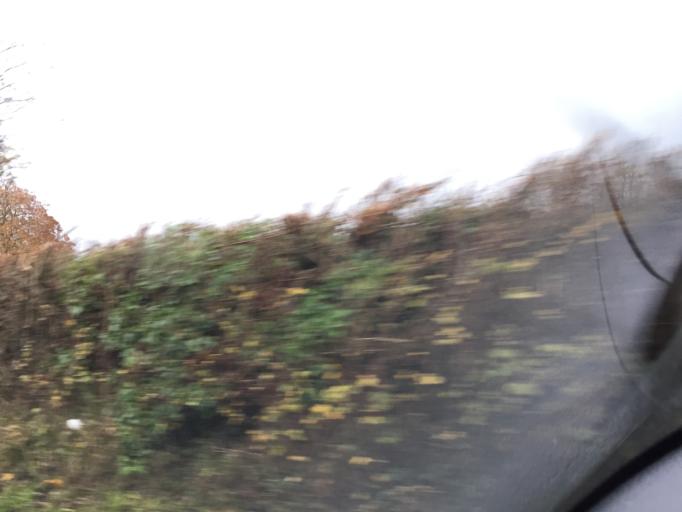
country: GB
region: England
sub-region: South Gloucestershire
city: Yate
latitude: 51.5154
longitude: -2.4154
